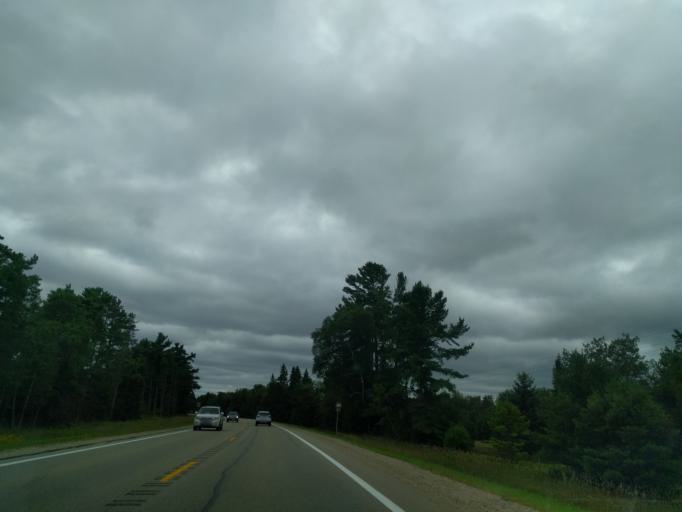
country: US
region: Michigan
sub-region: Delta County
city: Escanaba
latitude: 45.4832
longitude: -87.3057
